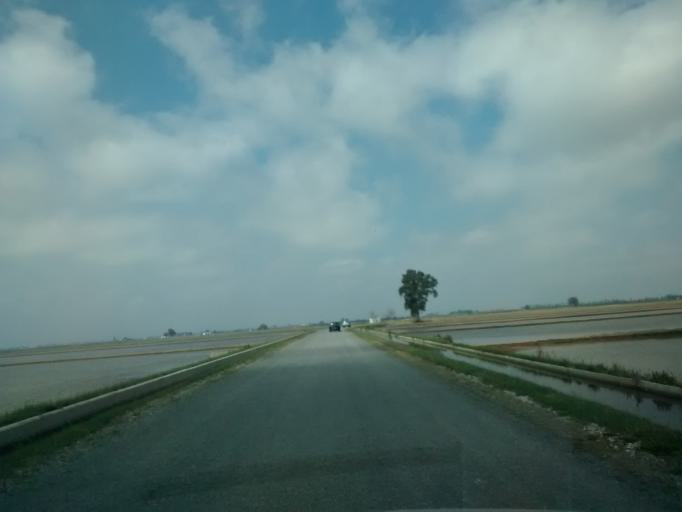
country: ES
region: Catalonia
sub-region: Provincia de Tarragona
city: Deltebre
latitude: 40.6789
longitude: 0.7983
